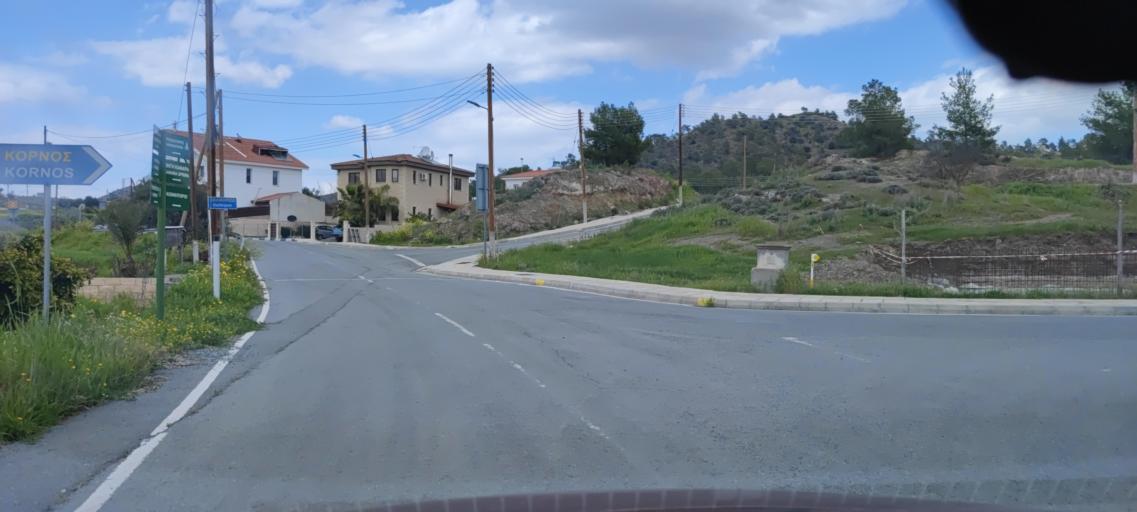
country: CY
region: Larnaka
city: Kornos
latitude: 34.9159
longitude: 33.3630
